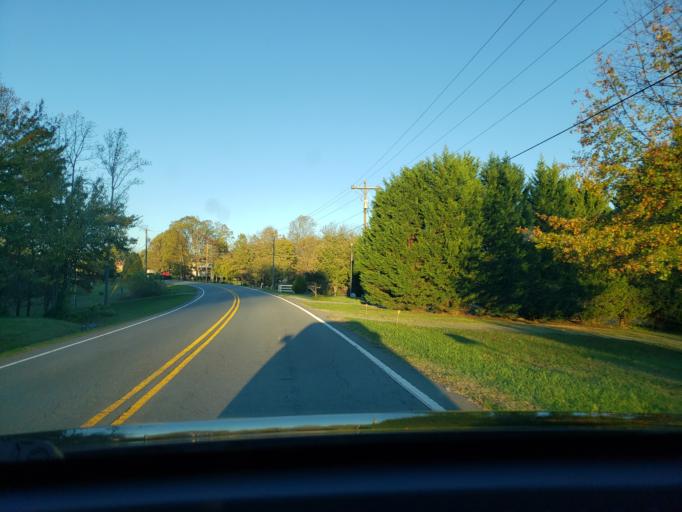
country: US
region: North Carolina
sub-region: Stokes County
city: Danbury
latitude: 36.3502
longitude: -80.2187
